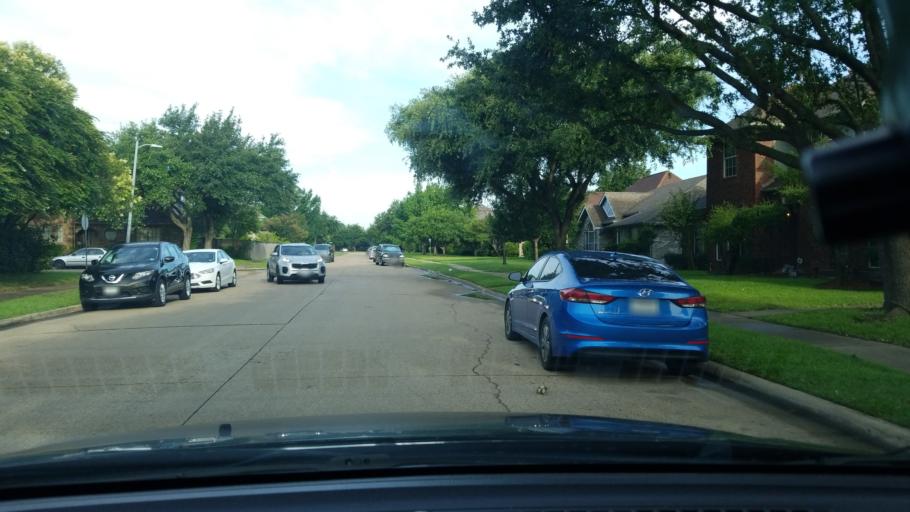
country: US
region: Texas
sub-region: Dallas County
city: Mesquite
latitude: 32.8009
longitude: -96.6017
